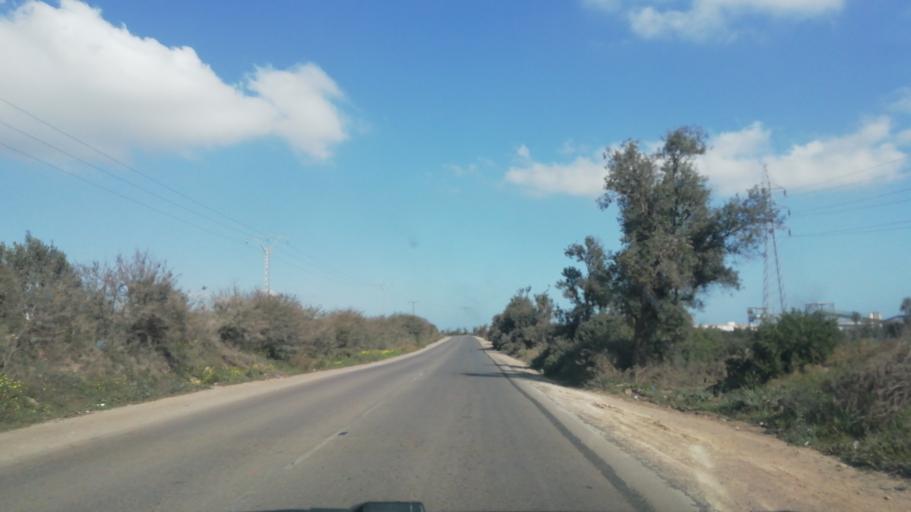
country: DZ
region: Oran
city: Ain el Bya
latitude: 35.7651
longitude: -0.2761
